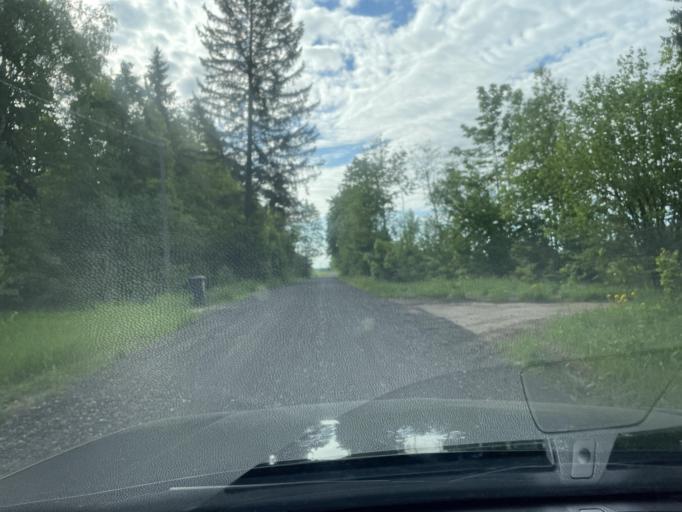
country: EE
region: Harju
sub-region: Keila linn
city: Keila
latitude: 59.3023
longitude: 24.3048
